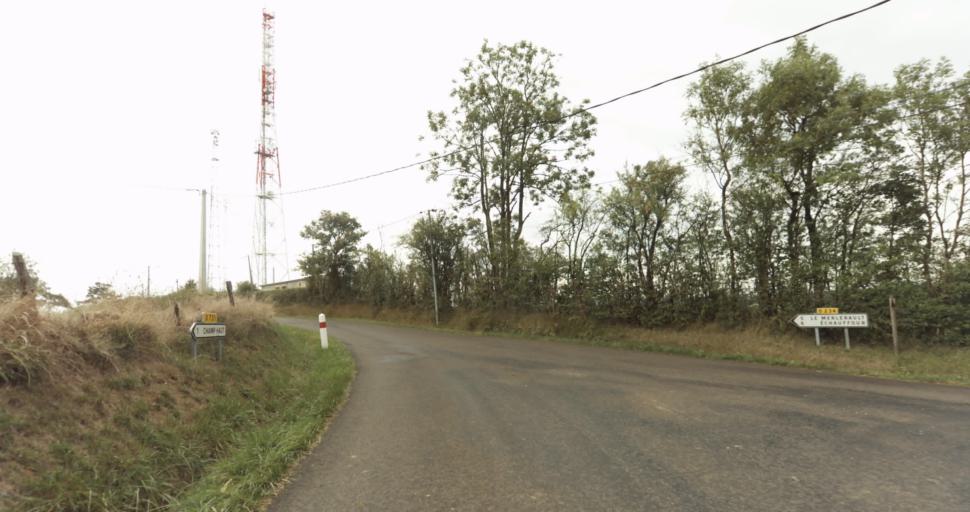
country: FR
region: Lower Normandy
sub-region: Departement de l'Orne
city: Gace
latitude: 48.7170
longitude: 0.3198
